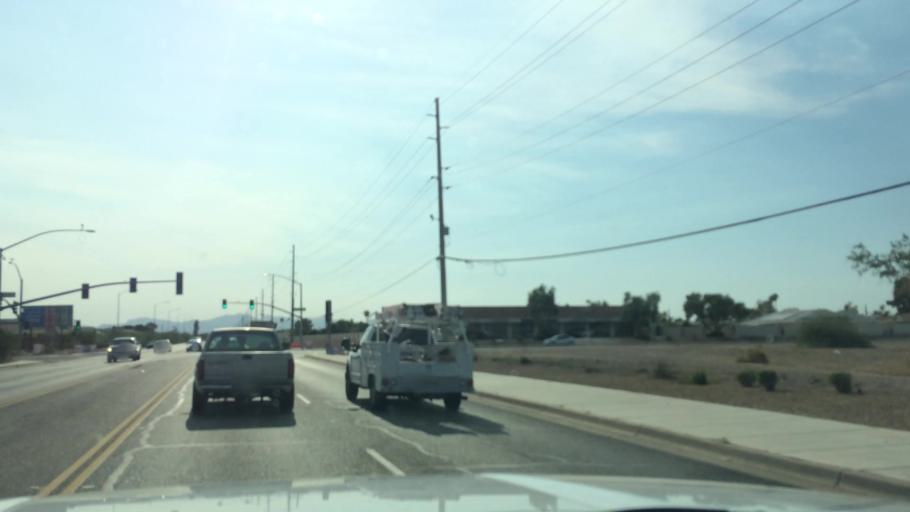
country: US
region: Arizona
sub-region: Maricopa County
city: Sun City
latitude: 33.5658
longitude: -112.2751
